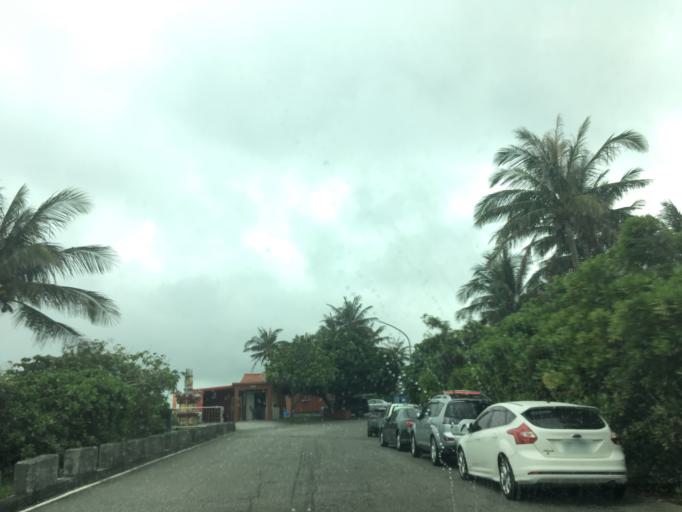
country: TW
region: Taiwan
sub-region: Taitung
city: Taitung
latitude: 22.7933
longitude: 121.1944
